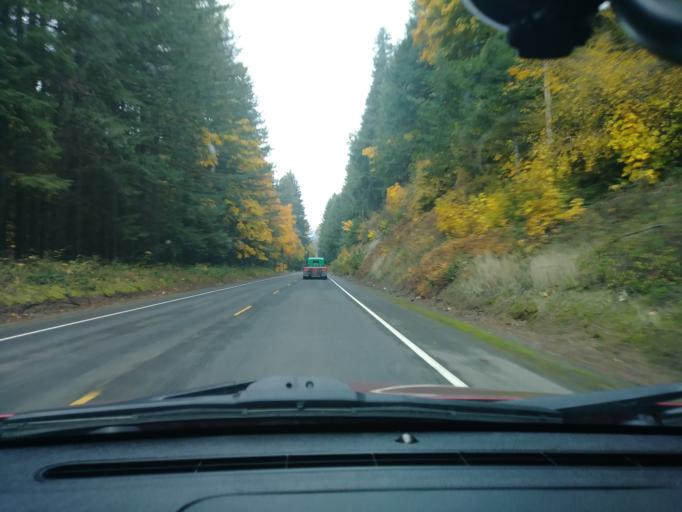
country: US
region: Oregon
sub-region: Washington County
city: Banks
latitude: 45.6521
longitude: -123.2865
